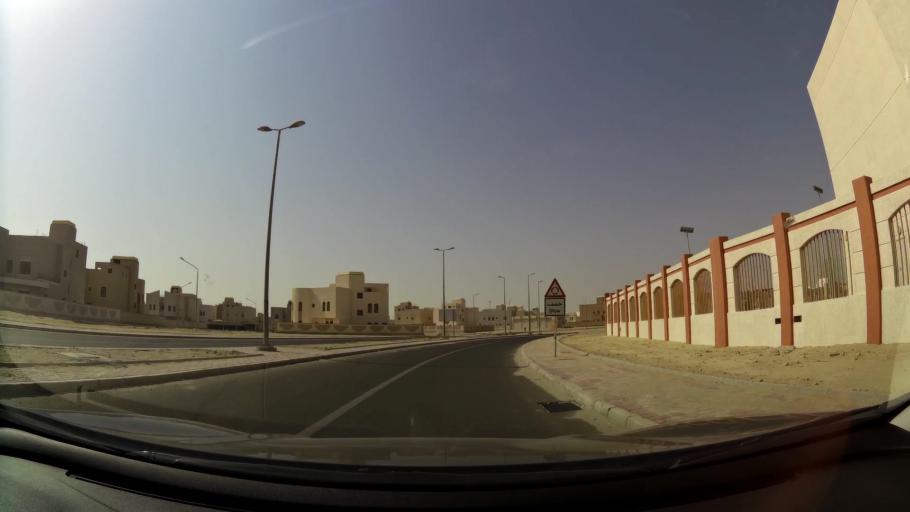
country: KW
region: Al Ahmadi
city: Al Wafrah
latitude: 28.7983
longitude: 48.0727
